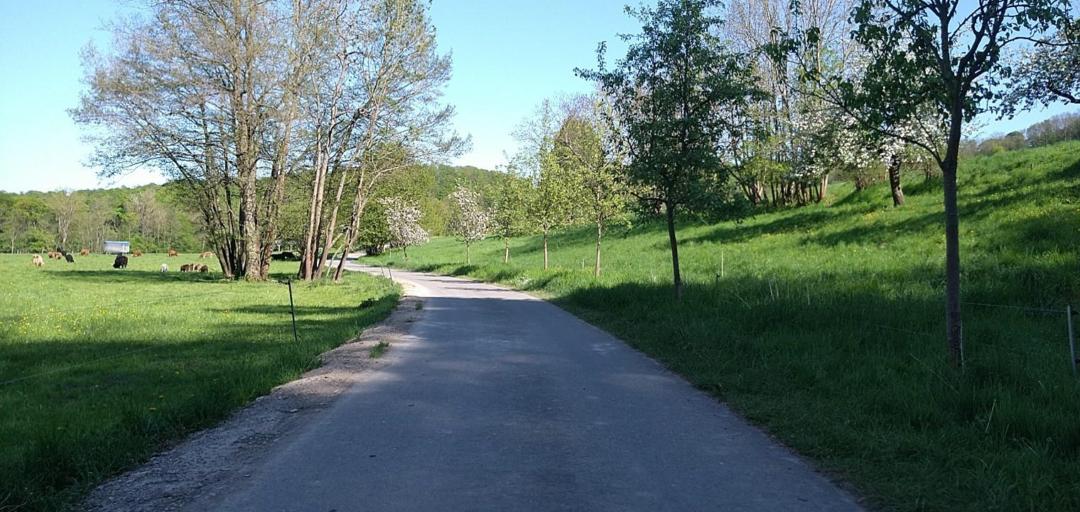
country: DE
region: Thuringia
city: Kiliansroda
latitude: 50.9207
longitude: 11.3662
